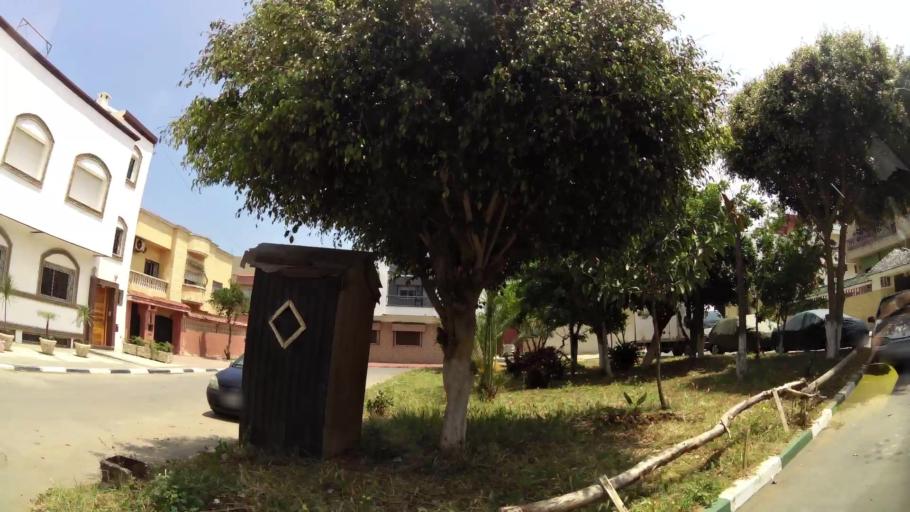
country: MA
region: Rabat-Sale-Zemmour-Zaer
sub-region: Skhirate-Temara
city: Temara
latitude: 33.9795
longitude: -6.8934
